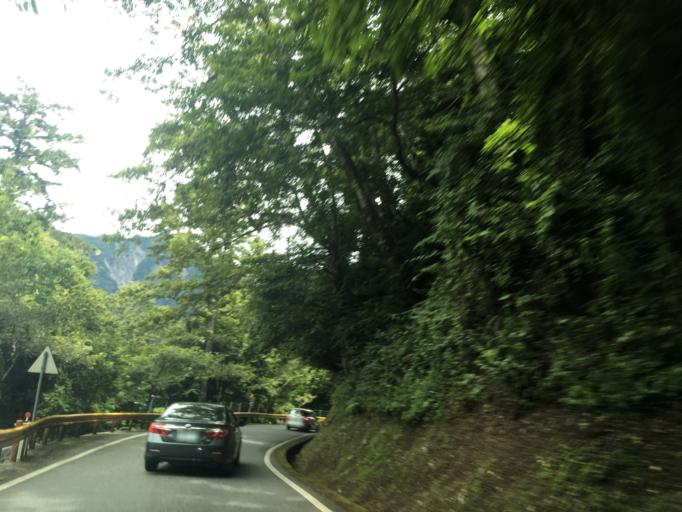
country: TW
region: Taiwan
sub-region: Hualien
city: Hualian
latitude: 24.1796
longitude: 121.3909
